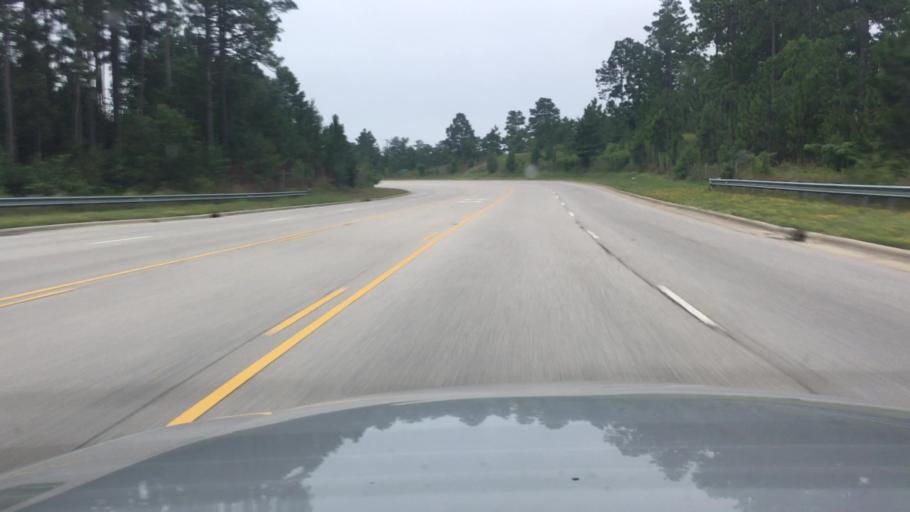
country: US
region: North Carolina
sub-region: Cumberland County
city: Fayetteville
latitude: 35.0144
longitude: -78.8890
